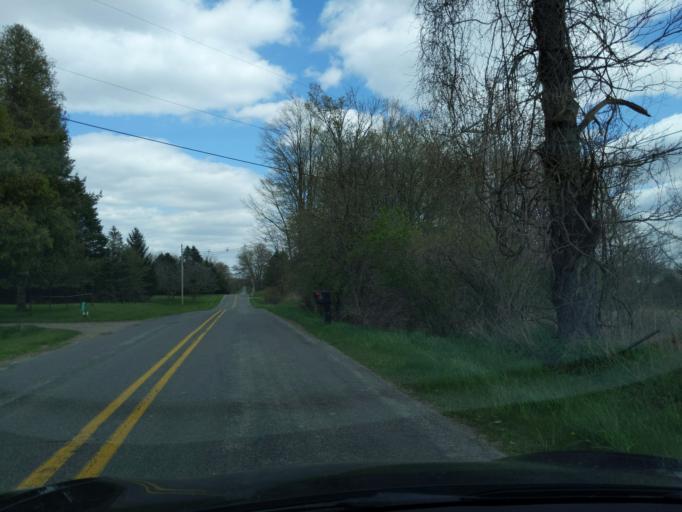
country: US
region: Michigan
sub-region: Ingham County
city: Holt
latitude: 42.6185
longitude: -84.5386
